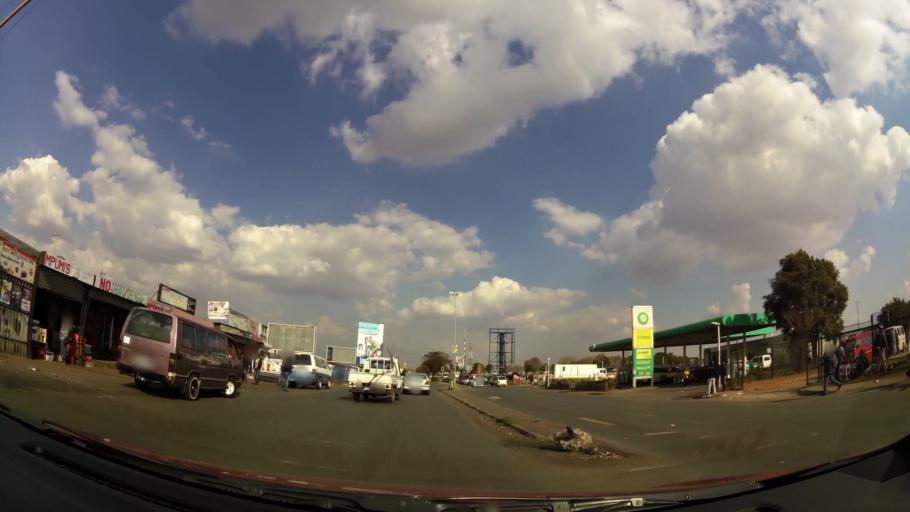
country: ZA
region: Gauteng
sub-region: City of Johannesburg Metropolitan Municipality
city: Roodepoort
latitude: -26.2125
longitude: 27.8706
